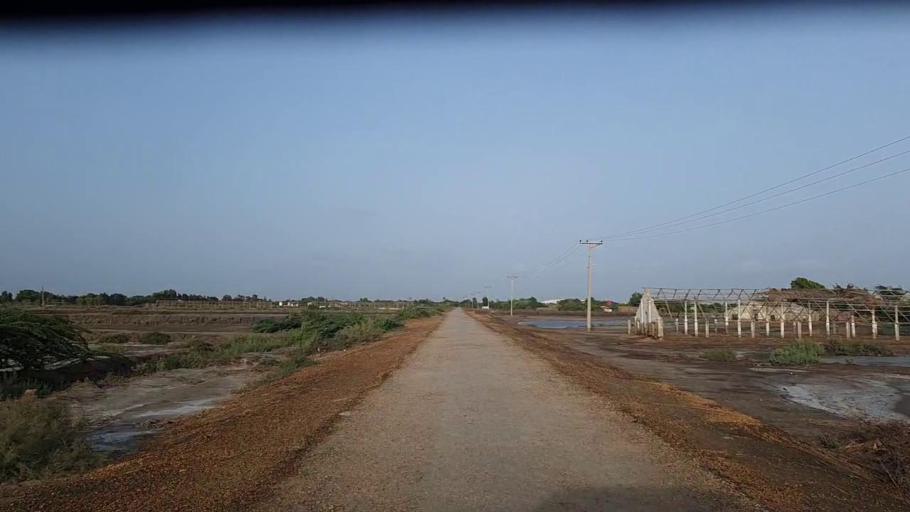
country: PK
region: Sindh
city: Thatta
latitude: 24.7601
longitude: 67.9089
